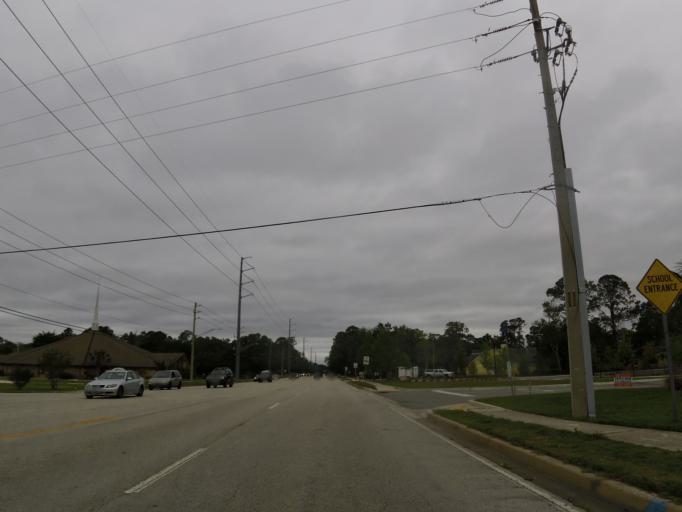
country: US
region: Florida
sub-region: Saint Johns County
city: Fruit Cove
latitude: 30.1768
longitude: -81.6046
